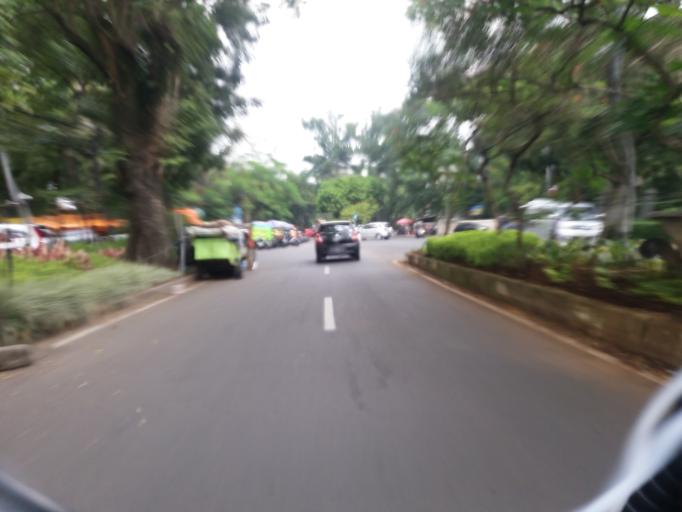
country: ID
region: West Java
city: Bandung
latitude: -6.9031
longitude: 107.6237
